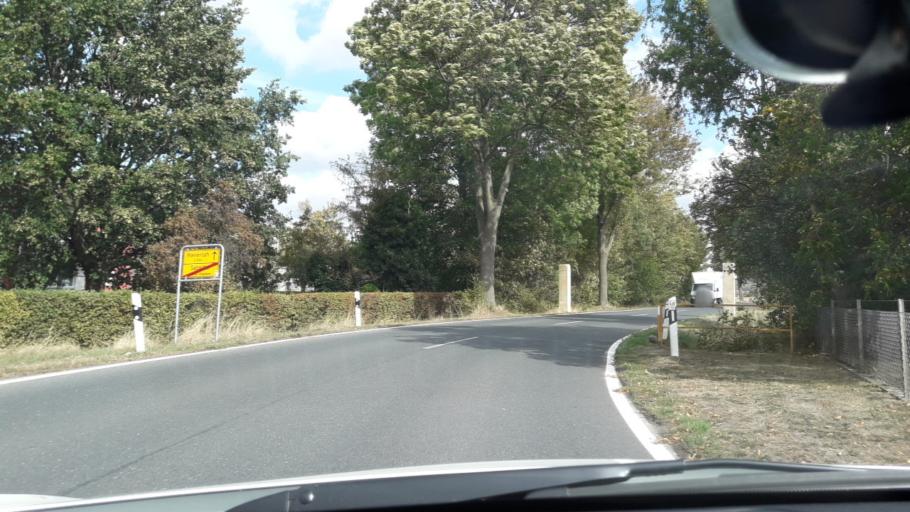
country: DE
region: Lower Saxony
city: Alt Wallmoden
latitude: 52.0427
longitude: 10.3109
